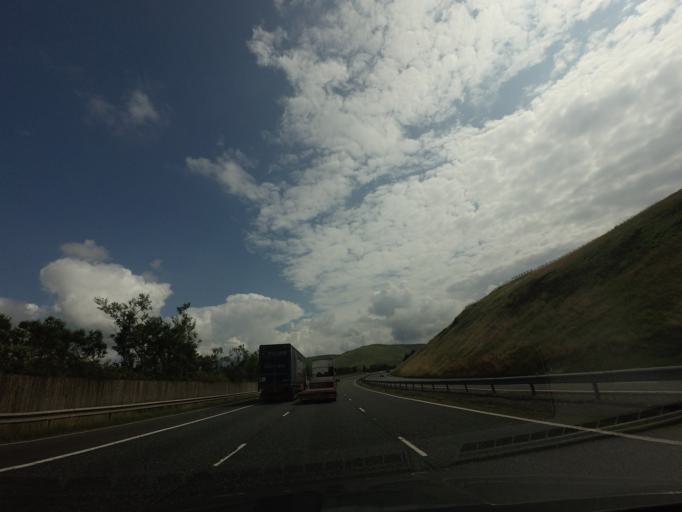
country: GB
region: Scotland
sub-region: South Lanarkshire
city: Biggar
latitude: 55.4643
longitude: -3.6505
